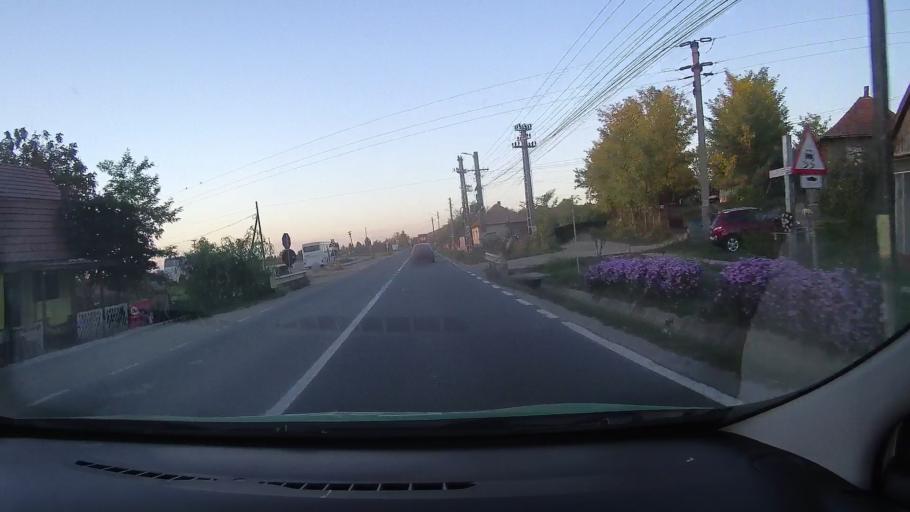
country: RO
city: Szekelyhid
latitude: 47.3587
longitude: 22.1117
